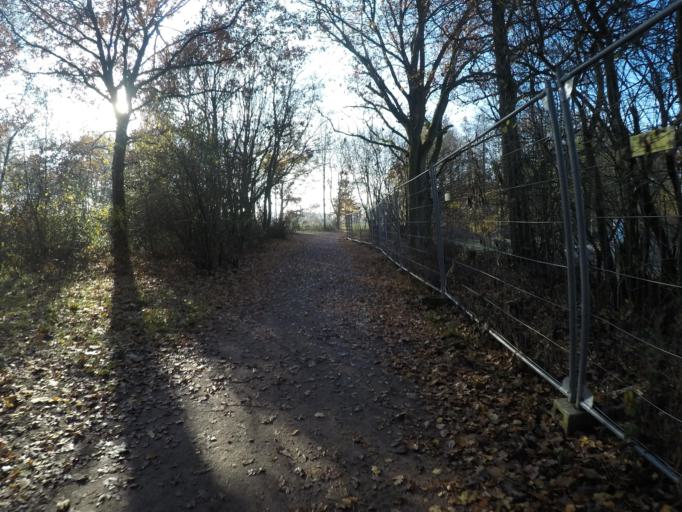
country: DE
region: Hamburg
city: Eidelstedt
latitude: 53.6212
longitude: 9.9246
